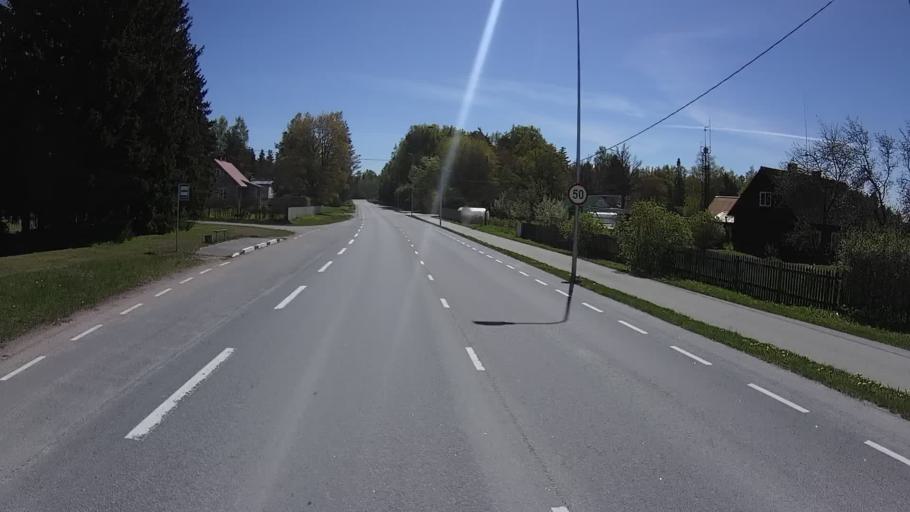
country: EE
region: Harju
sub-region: Raasiku vald
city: Raasiku
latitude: 59.1769
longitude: 25.1694
